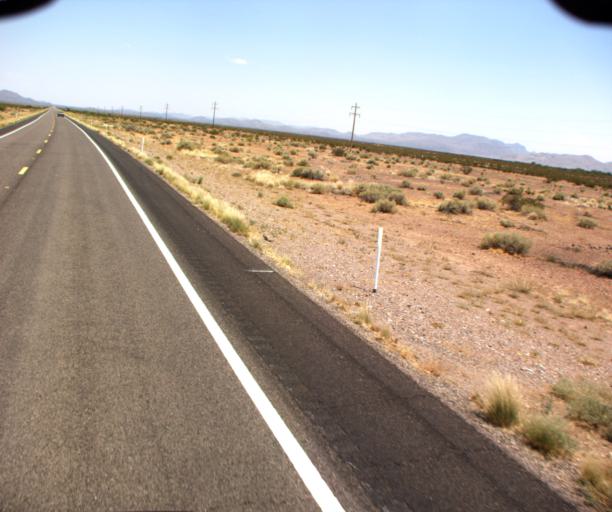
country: US
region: Arizona
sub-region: Graham County
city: Safford
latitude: 32.7817
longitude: -109.5331
